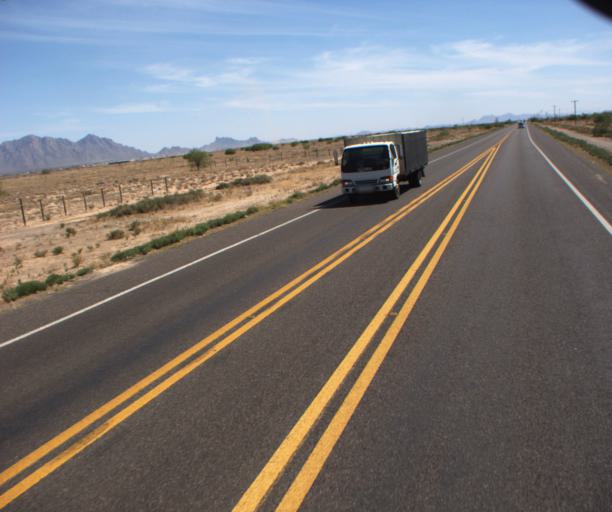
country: US
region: Arizona
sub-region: Pinal County
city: Eloy
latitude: 32.8201
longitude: -111.5154
